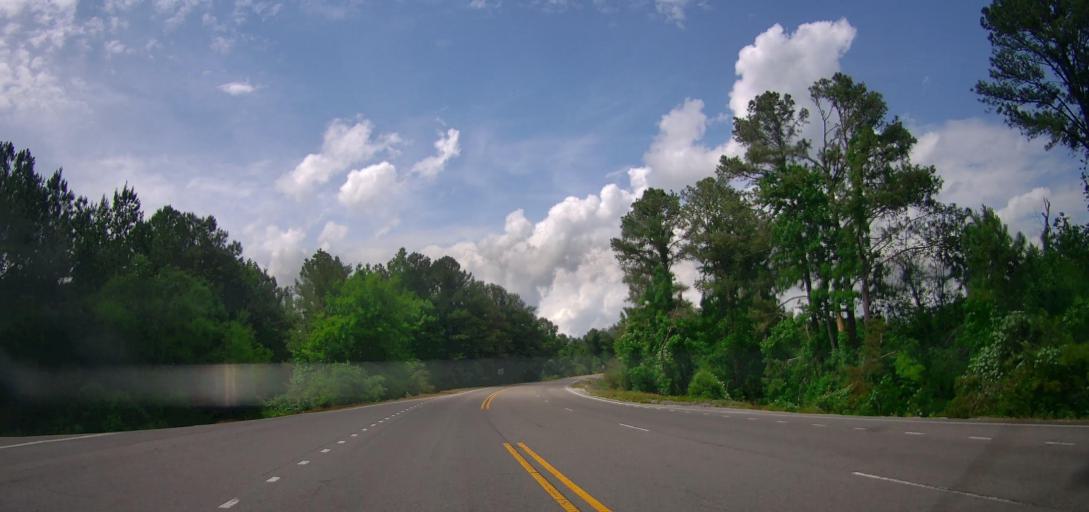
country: US
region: Alabama
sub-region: Marion County
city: Hamilton
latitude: 34.0739
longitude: -87.9769
